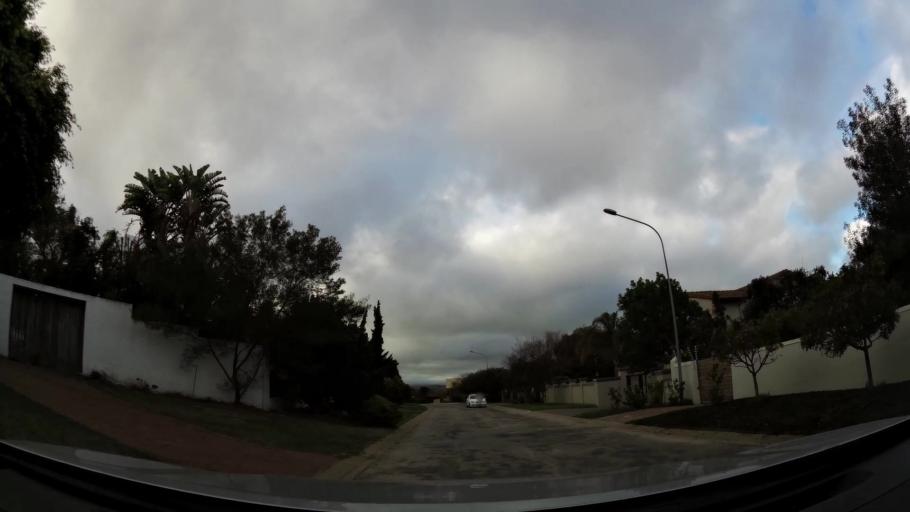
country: ZA
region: Western Cape
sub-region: Eden District Municipality
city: Plettenberg Bay
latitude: -34.0488
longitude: 23.3649
